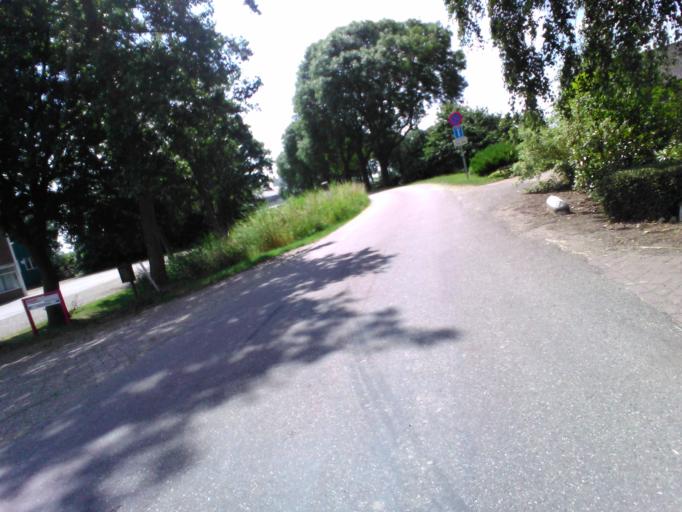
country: NL
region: North Brabant
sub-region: Gemeente Waalwijk
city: Waspik
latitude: 51.7270
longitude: 4.9617
